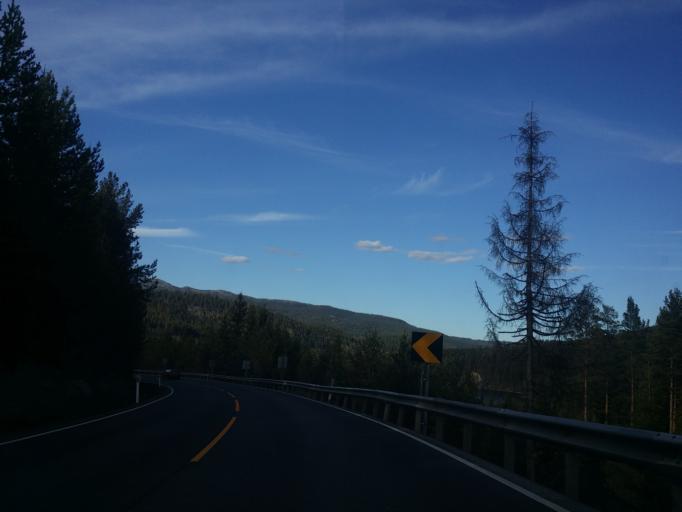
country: NO
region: Buskerud
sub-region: Kongsberg
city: Kongsberg
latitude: 59.6191
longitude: 9.4736
